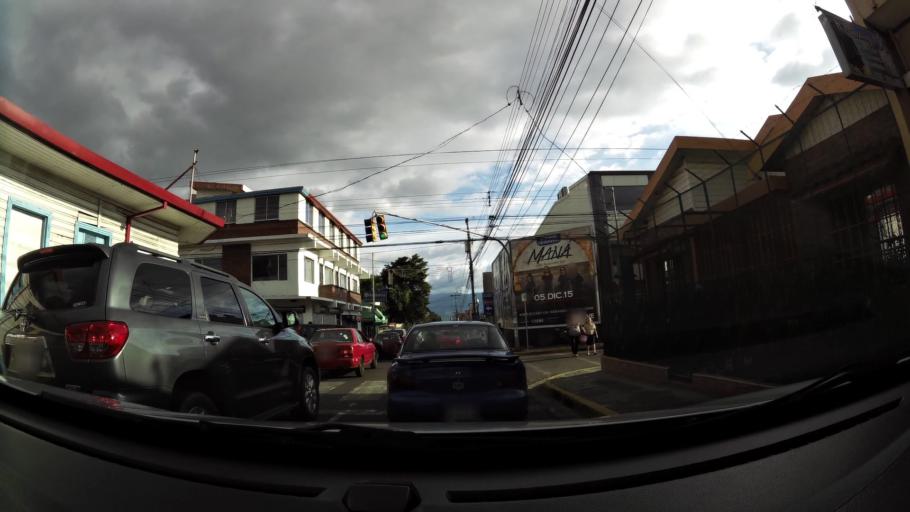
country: CR
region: Alajuela
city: Alajuela
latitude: 10.0126
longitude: -84.2141
